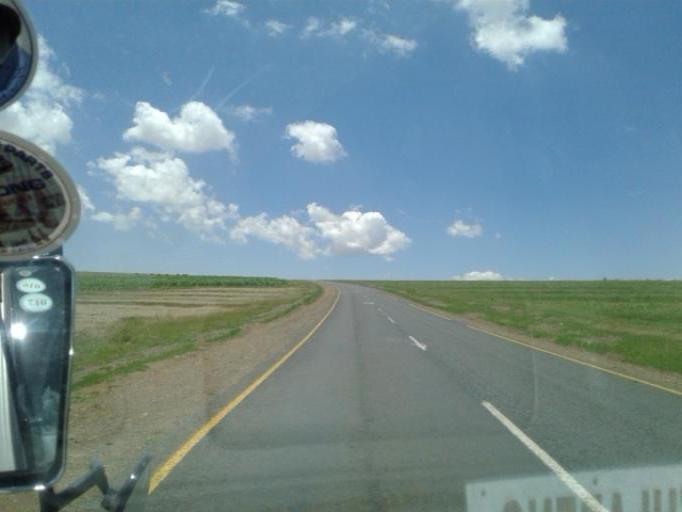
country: LS
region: Maseru
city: Maseru
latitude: -29.3055
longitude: 27.6080
